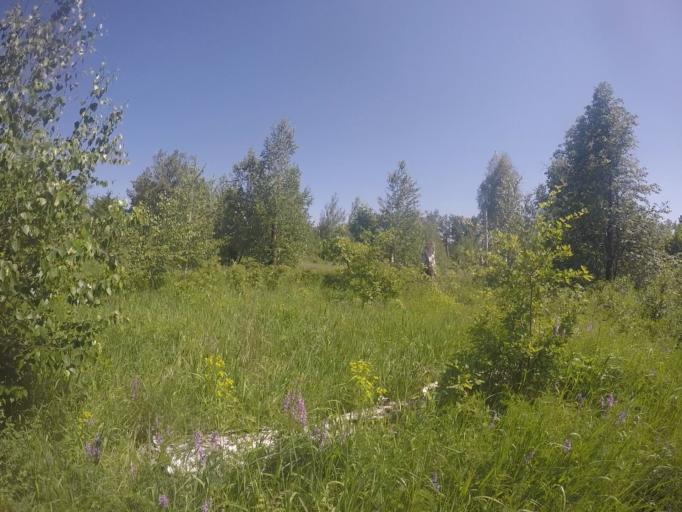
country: RU
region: Saratov
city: Krasnyy Oktyabr'
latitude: 51.3091
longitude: 45.5782
